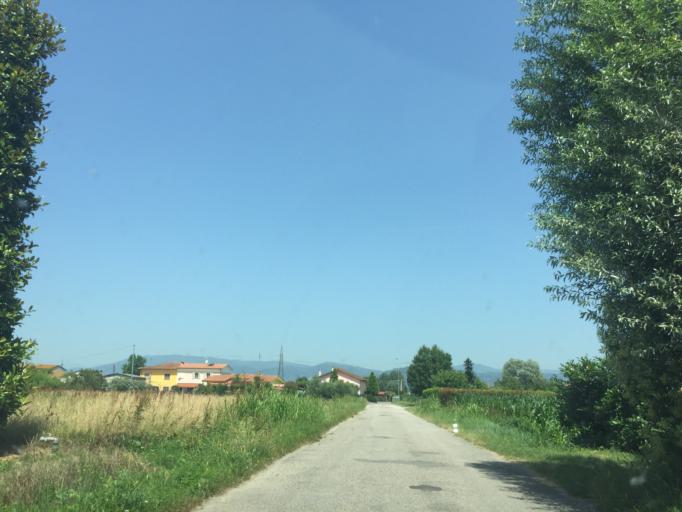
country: IT
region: Tuscany
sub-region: Provincia di Pistoia
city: Anchione
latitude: 43.8333
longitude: 10.7553
